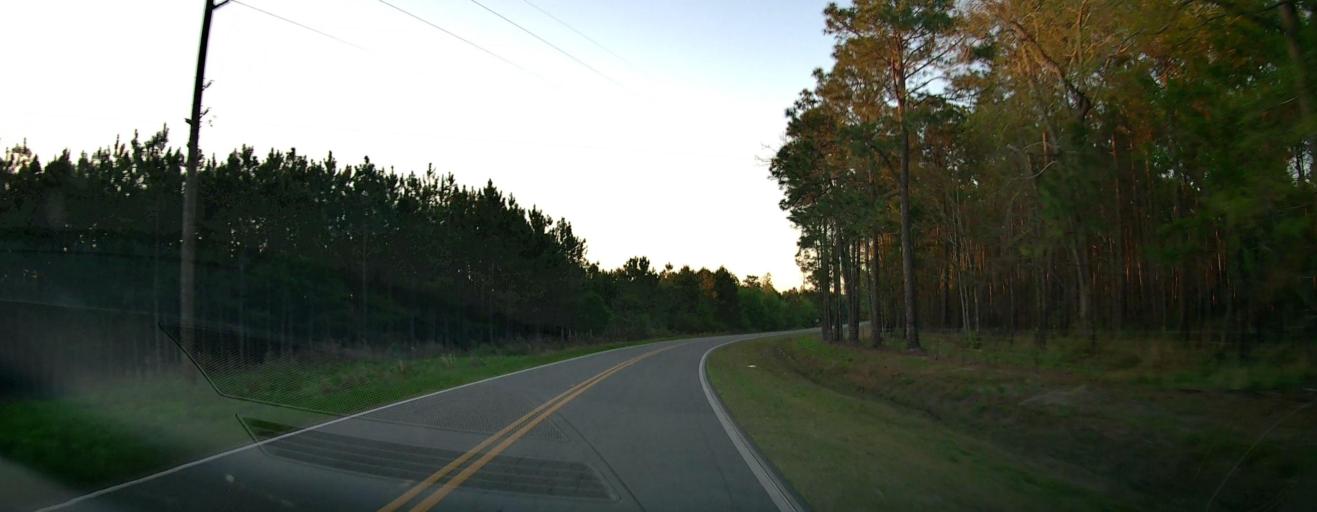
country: US
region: Georgia
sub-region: Ben Hill County
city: Fitzgerald
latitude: 31.7588
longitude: -83.3548
